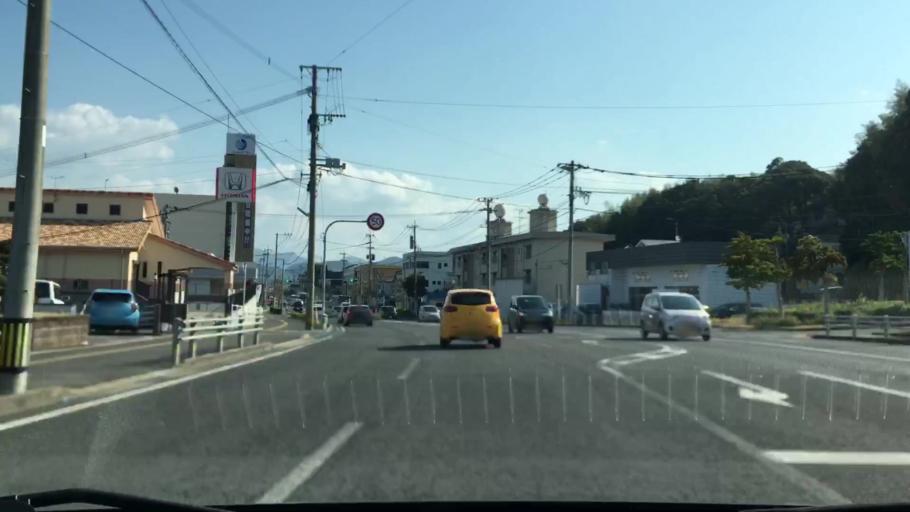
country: JP
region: Nagasaki
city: Togitsu
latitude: 32.8467
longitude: 129.8311
